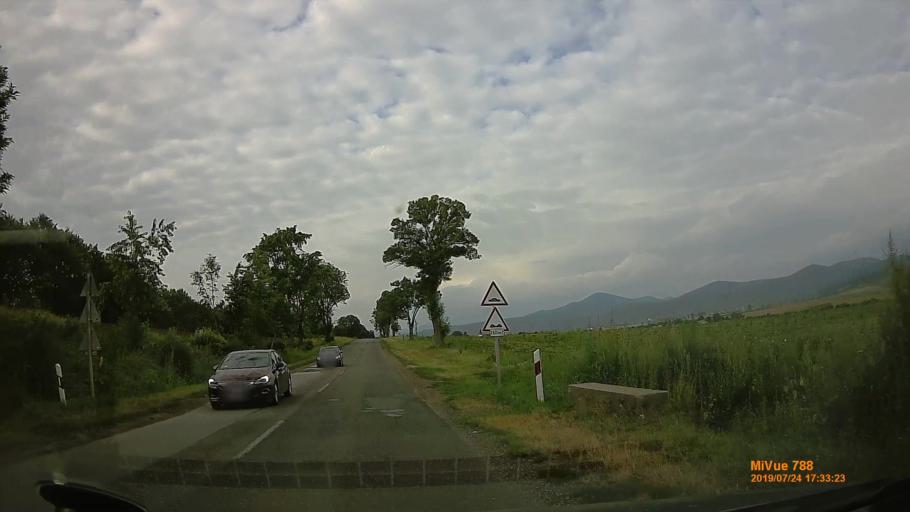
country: HU
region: Borsod-Abauj-Zemplen
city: Abaujszanto
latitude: 48.2932
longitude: 21.1902
